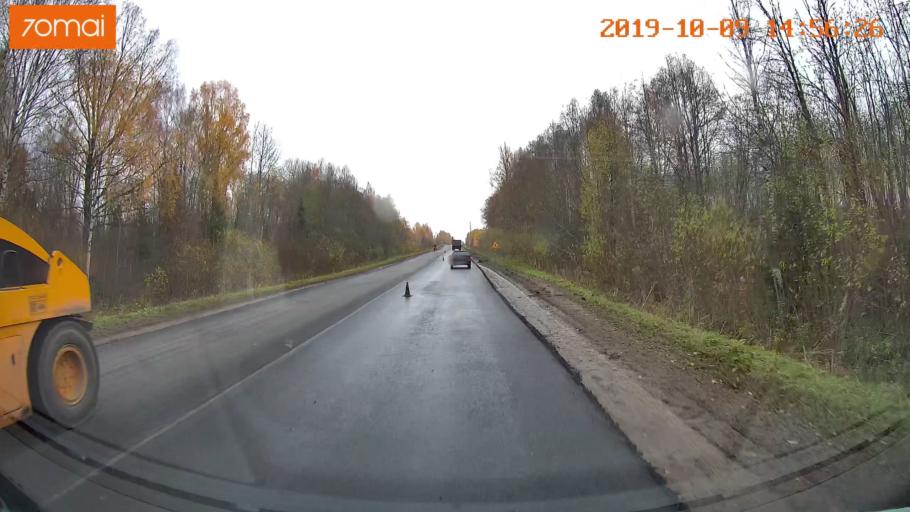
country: RU
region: Kostroma
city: Chistyye Bory
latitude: 58.3458
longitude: 41.6473
